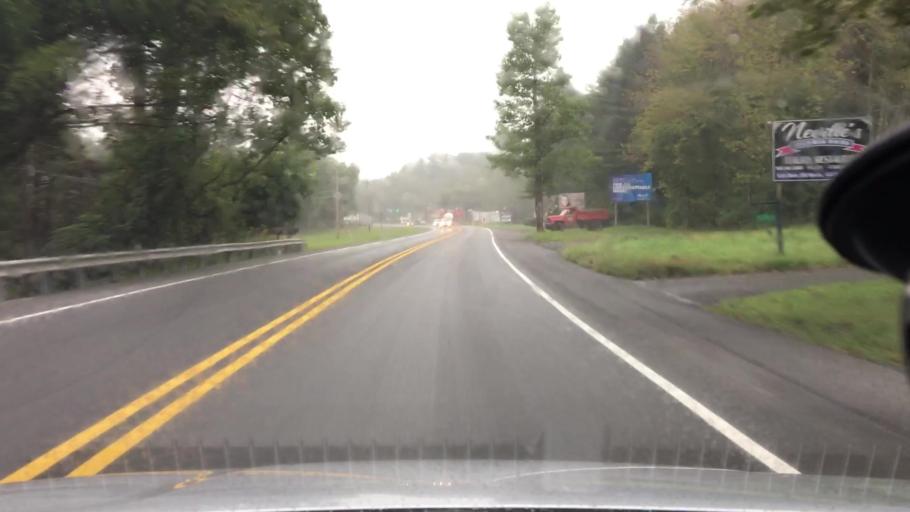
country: US
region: Pennsylvania
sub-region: Monroe County
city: Mount Pocono
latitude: 41.1282
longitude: -75.3141
